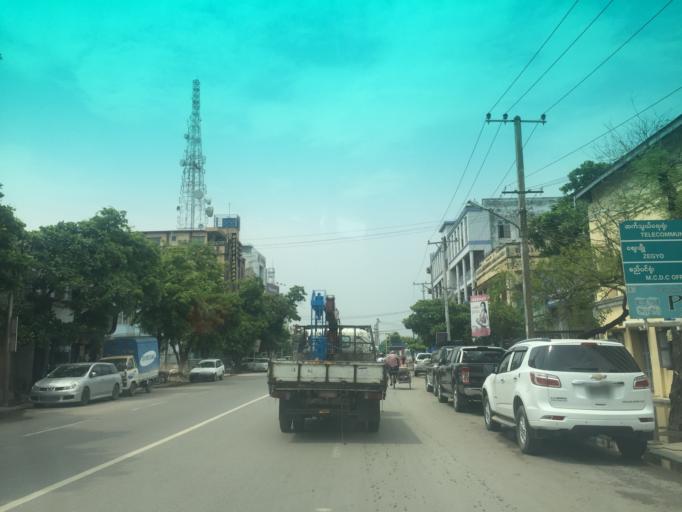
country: MM
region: Mandalay
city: Mandalay
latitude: 21.9821
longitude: 96.0844
